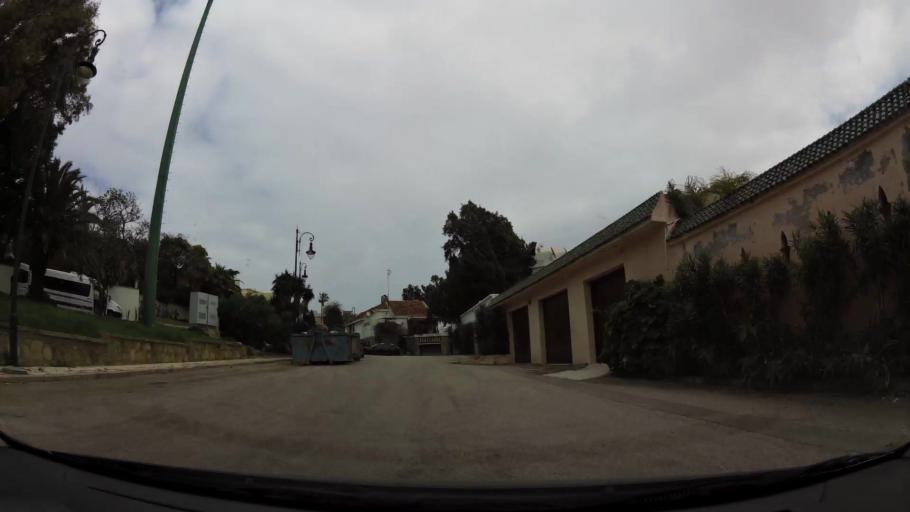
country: MA
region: Tanger-Tetouan
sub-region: Tanger-Assilah
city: Tangier
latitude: 35.7853
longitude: -5.8485
